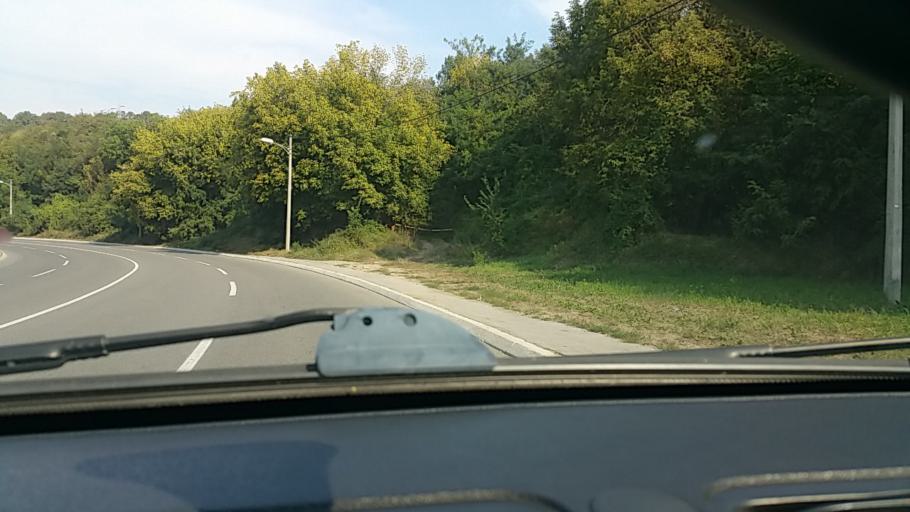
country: RS
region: Central Serbia
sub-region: Belgrade
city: Rakovica
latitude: 44.7349
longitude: 20.4476
